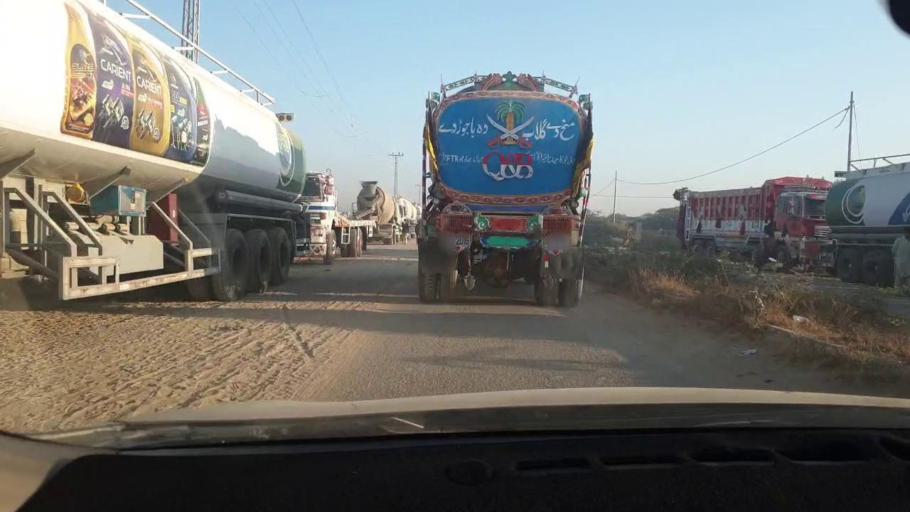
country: PK
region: Sindh
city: Malir Cantonment
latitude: 25.0157
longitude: 67.1708
